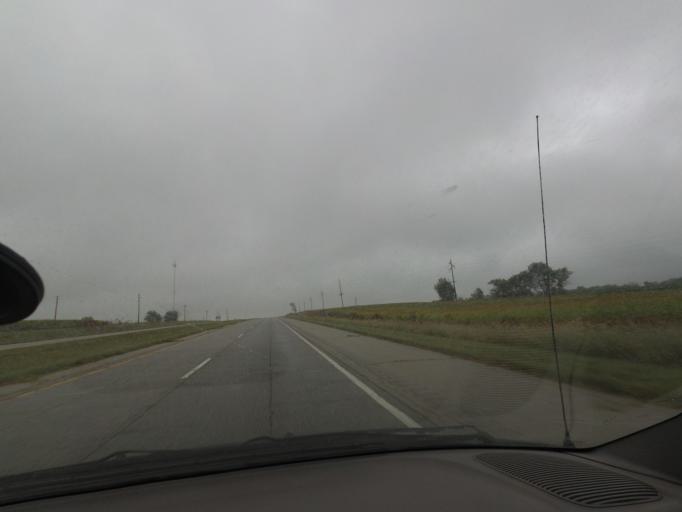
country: US
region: Illinois
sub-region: Pike County
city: Barry
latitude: 39.6995
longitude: -91.0218
